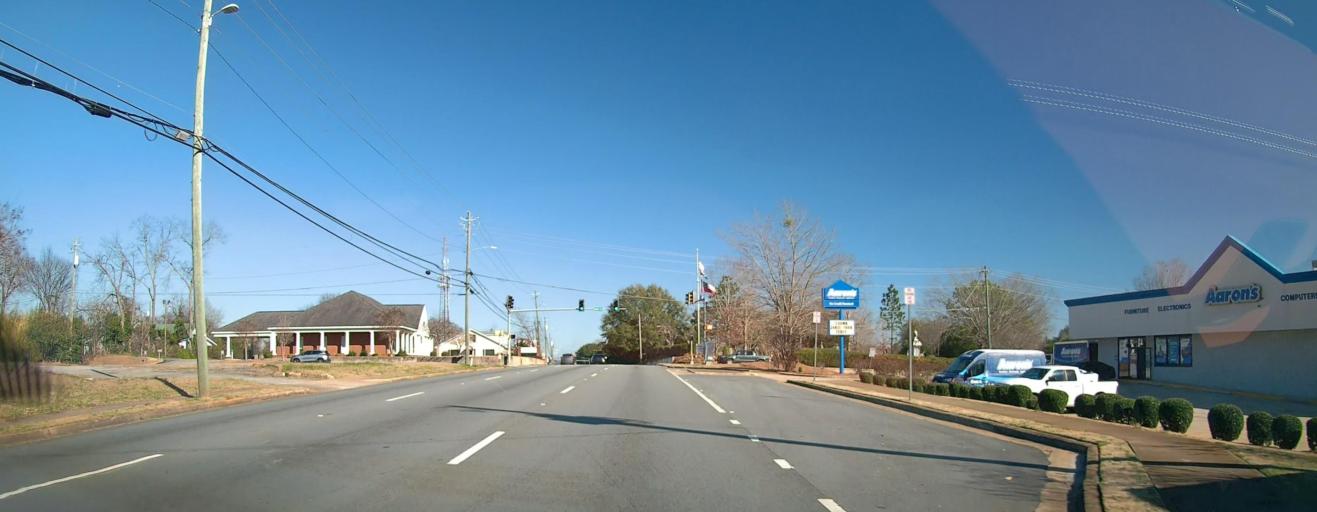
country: US
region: Georgia
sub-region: Sumter County
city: Americus
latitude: 32.0714
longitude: -84.2242
